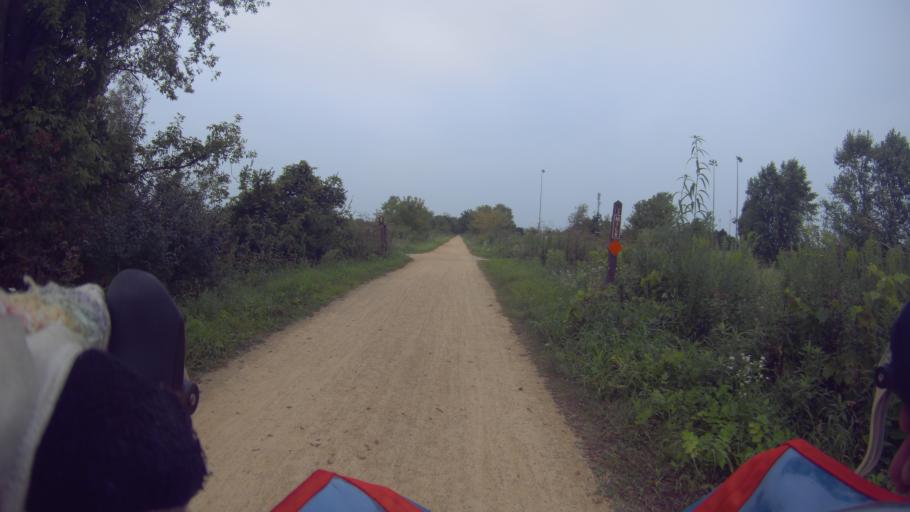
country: US
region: Wisconsin
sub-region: Dane County
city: Verona
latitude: 42.9916
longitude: -89.5187
